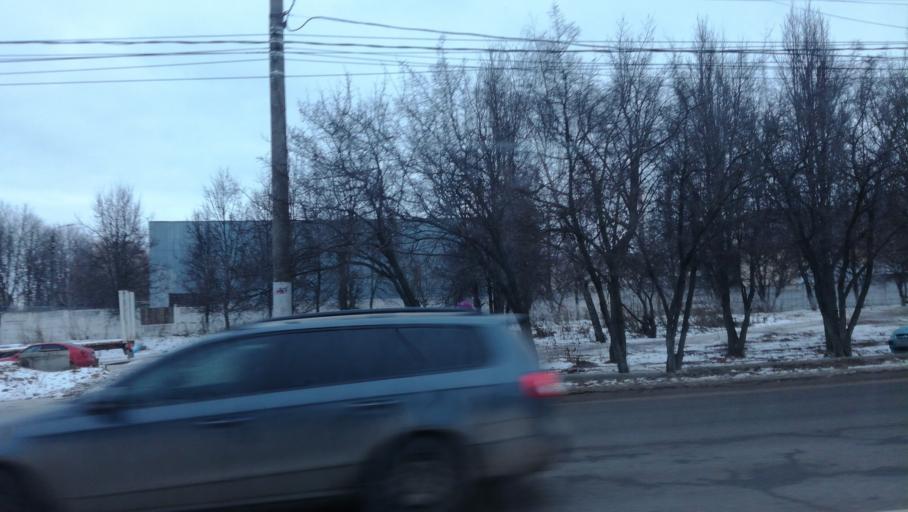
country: RU
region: Tula
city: Kosaya Gora
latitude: 54.1883
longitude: 37.5330
